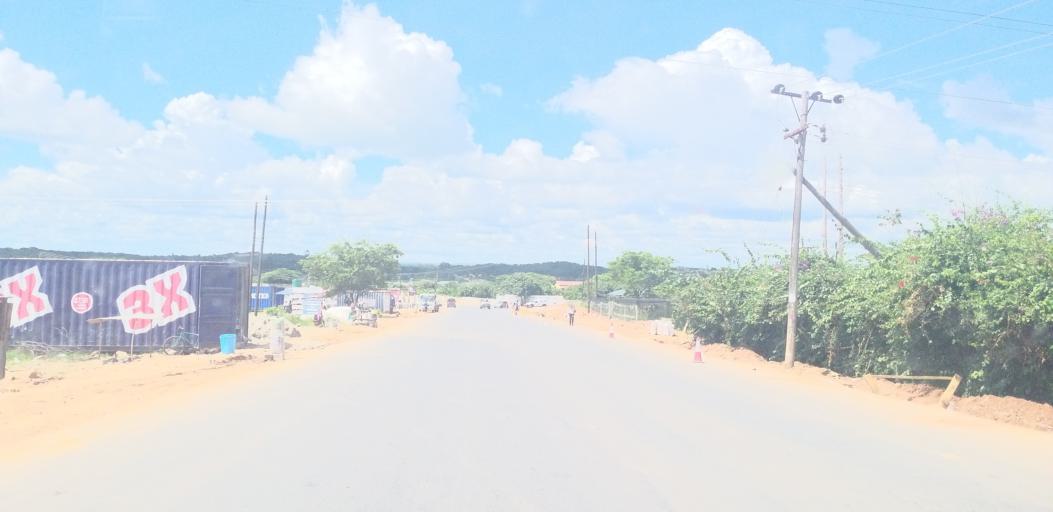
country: ZM
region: Lusaka
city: Lusaka
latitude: -15.3441
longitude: 28.3277
